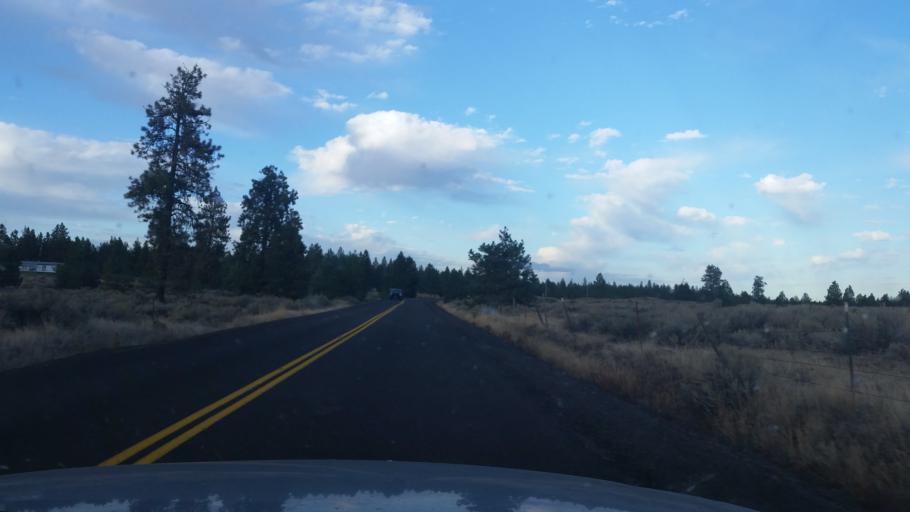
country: US
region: Washington
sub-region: Spokane County
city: Medical Lake
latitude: 47.4511
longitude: -117.8177
